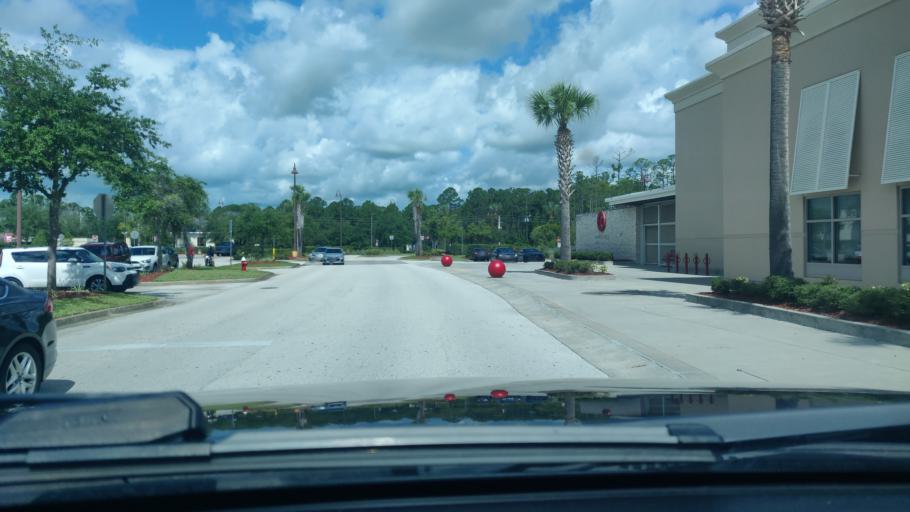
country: US
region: Florida
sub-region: Flagler County
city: Bunnell
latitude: 29.4772
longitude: -81.2193
